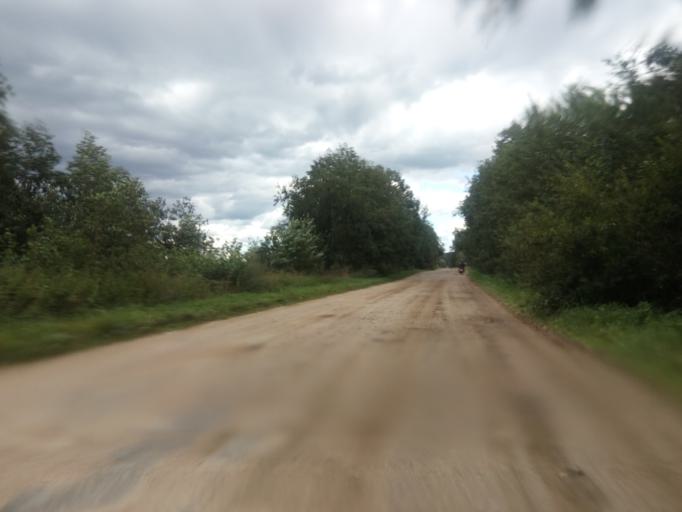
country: BY
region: Vitebsk
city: Dzisna
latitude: 55.7079
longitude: 28.3150
